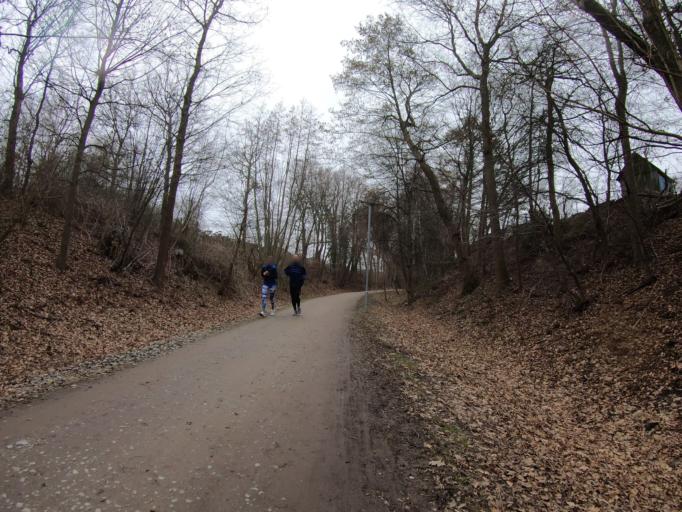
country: DE
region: Lower Saxony
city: Braunschweig
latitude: 52.2411
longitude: 10.4989
